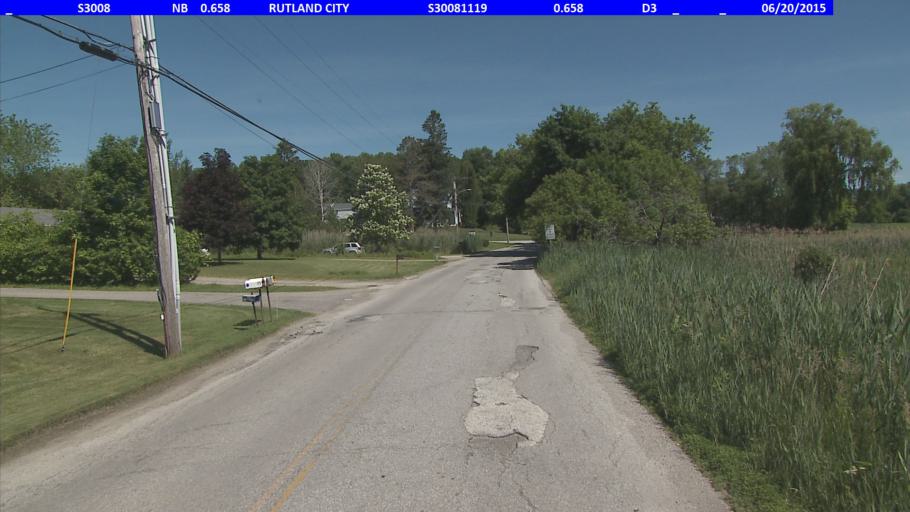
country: US
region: Vermont
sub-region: Rutland County
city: Rutland
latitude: 43.5959
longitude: -72.9936
